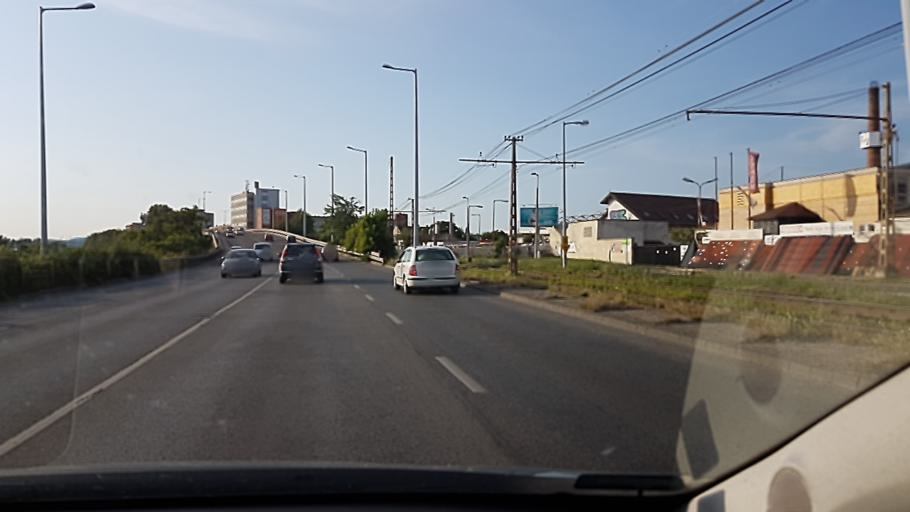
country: HU
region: Budapest
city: Budapest XX. keruelet
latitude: 47.4282
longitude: 19.1026
